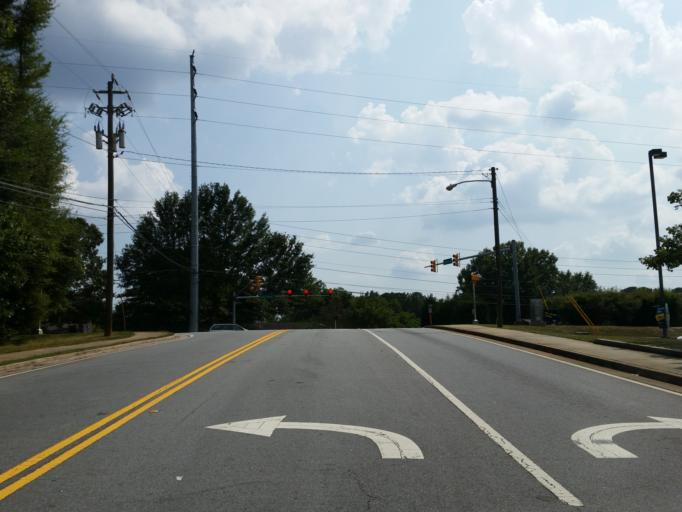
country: US
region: Georgia
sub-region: Cherokee County
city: Woodstock
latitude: 34.0258
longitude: -84.4810
